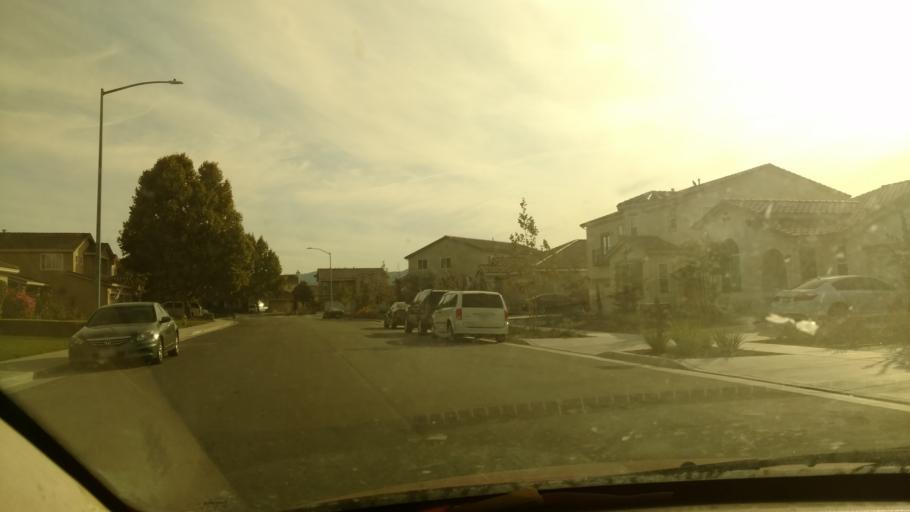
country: US
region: California
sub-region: San Benito County
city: Hollister
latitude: 36.8424
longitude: -121.3899
